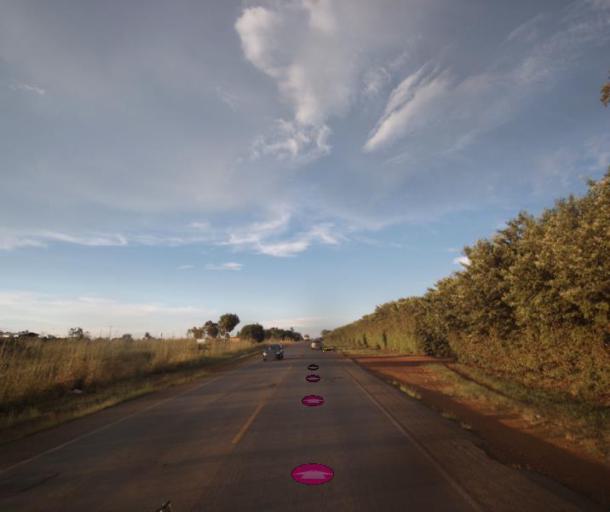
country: BR
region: Goias
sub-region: Anapolis
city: Anapolis
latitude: -16.2115
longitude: -48.9168
